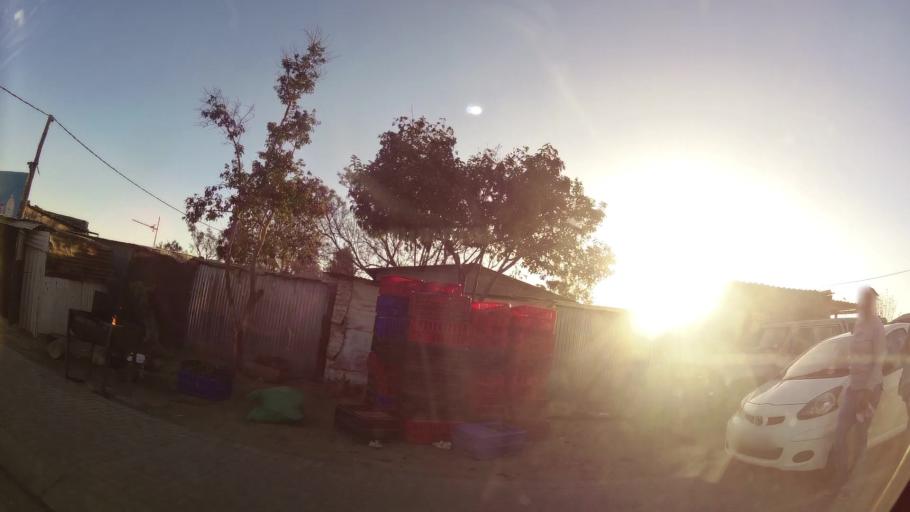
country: ZA
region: Gauteng
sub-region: City of Johannesburg Metropolitan Municipality
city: Diepsloot
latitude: -25.9227
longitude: 28.0156
